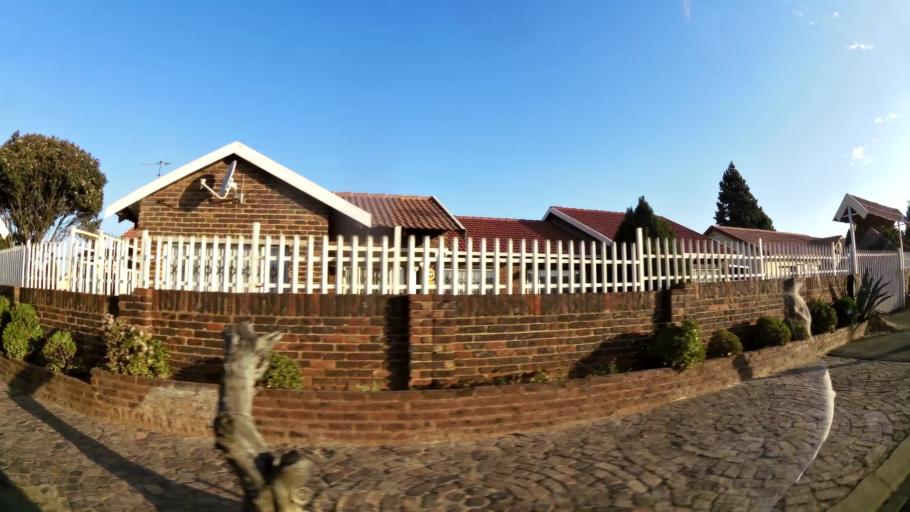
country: ZA
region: Gauteng
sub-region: West Rand District Municipality
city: Randfontein
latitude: -26.2040
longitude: 27.6537
